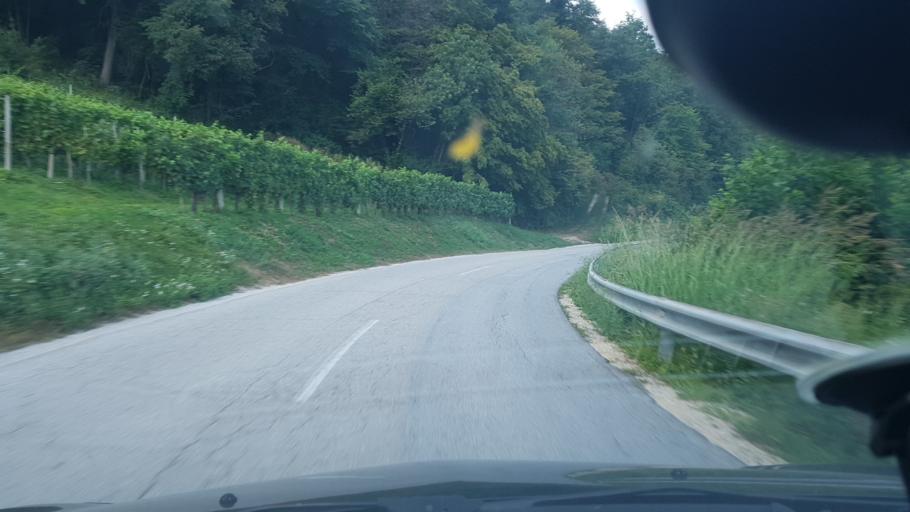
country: SI
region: Kozje
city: Kozje
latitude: 46.0411
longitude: 15.5776
